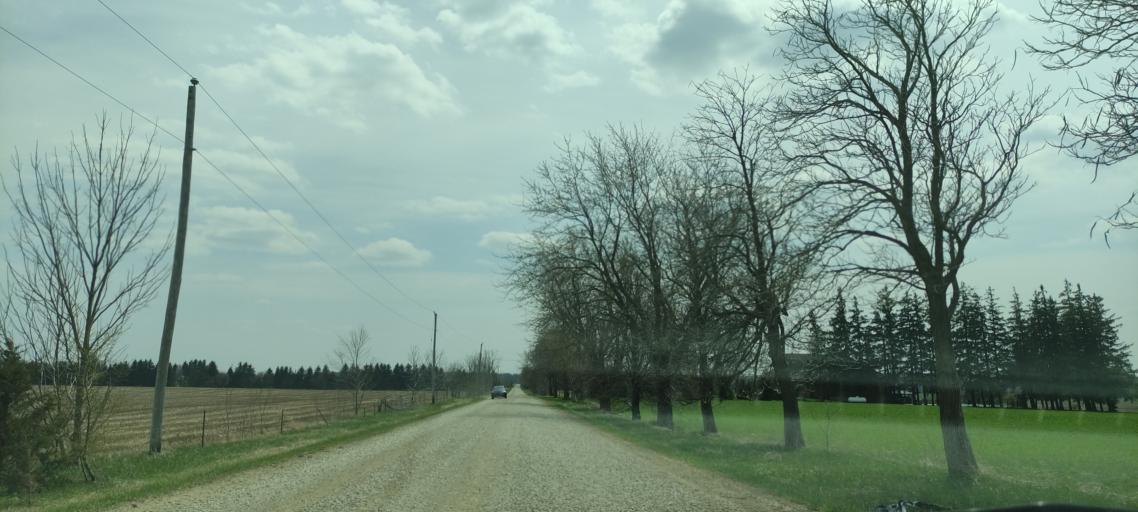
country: CA
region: Ontario
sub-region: Oxford County
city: Woodstock
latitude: 43.3422
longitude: -80.7414
